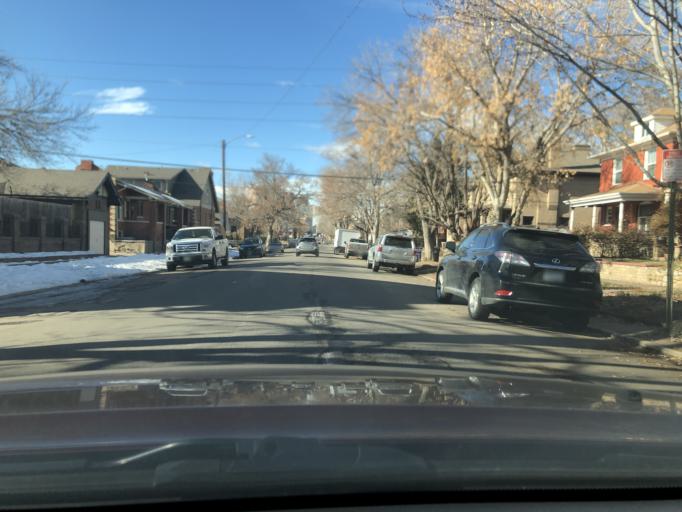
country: US
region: Colorado
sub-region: Denver County
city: Denver
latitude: 39.7482
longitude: -104.9611
